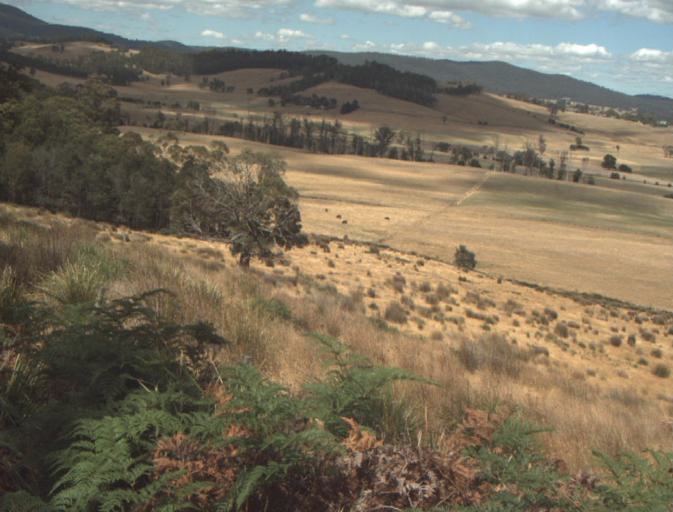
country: AU
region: Tasmania
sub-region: Launceston
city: Mayfield
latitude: -41.2058
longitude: 147.1551
